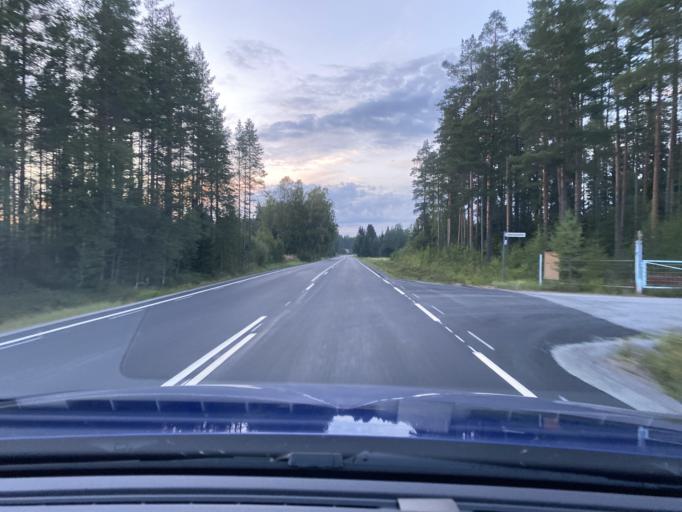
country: FI
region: Satakunta
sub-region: Pohjois-Satakunta
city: Honkajoki
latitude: 62.0709
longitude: 22.2499
